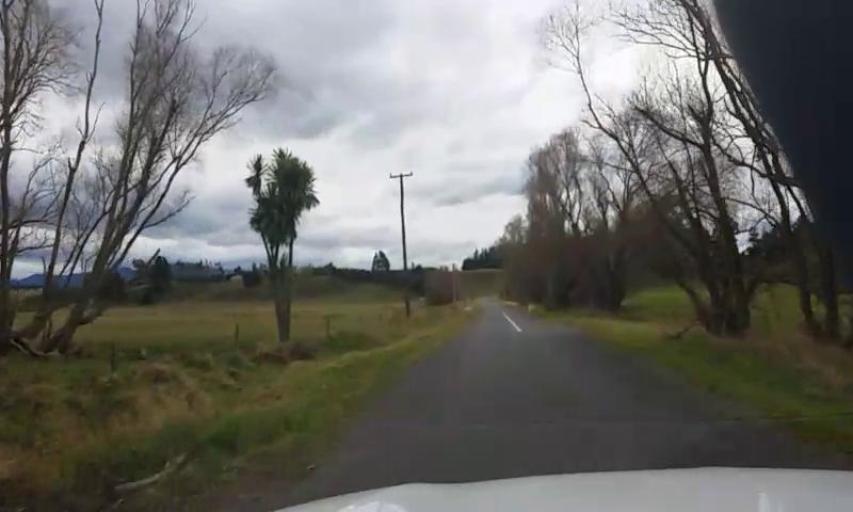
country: NZ
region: Canterbury
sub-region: Waimakariri District
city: Kaiapoi
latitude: -43.3024
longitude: 172.4379
